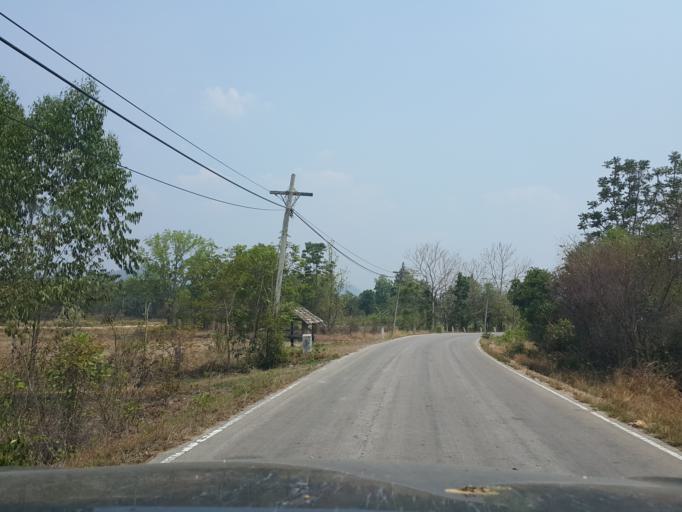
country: TH
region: Lampang
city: Mae Phrik
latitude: 17.5188
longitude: 99.1471
